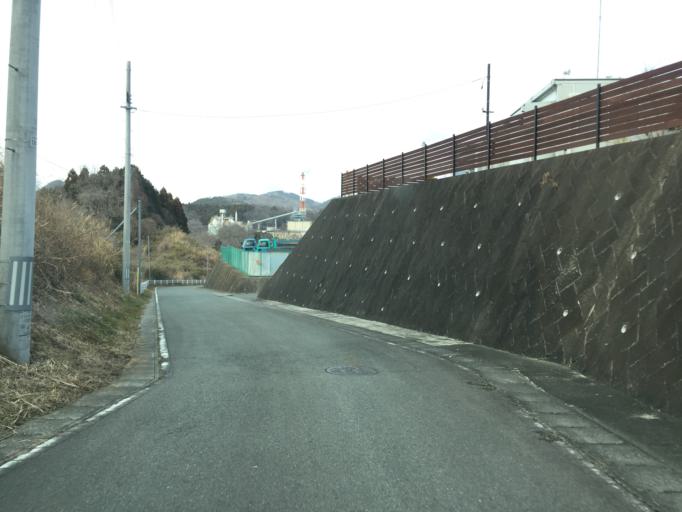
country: JP
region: Ibaraki
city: Kitaibaraki
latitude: 36.9343
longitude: 140.7423
